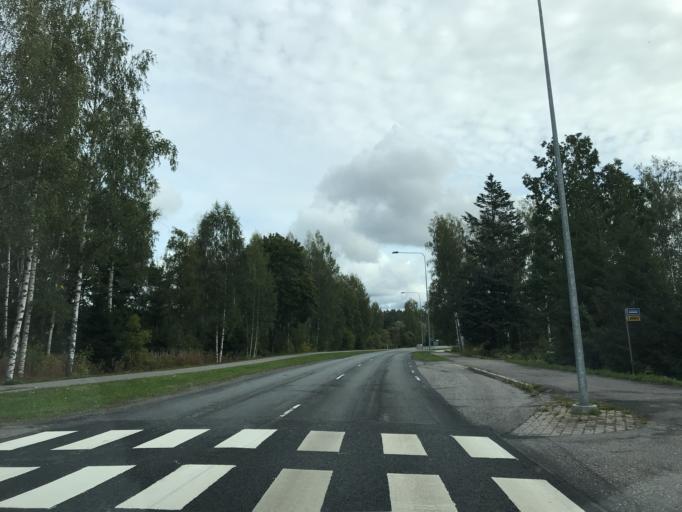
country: FI
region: Paijanne Tavastia
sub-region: Lahti
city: Lahti
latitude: 61.0110
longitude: 25.7838
